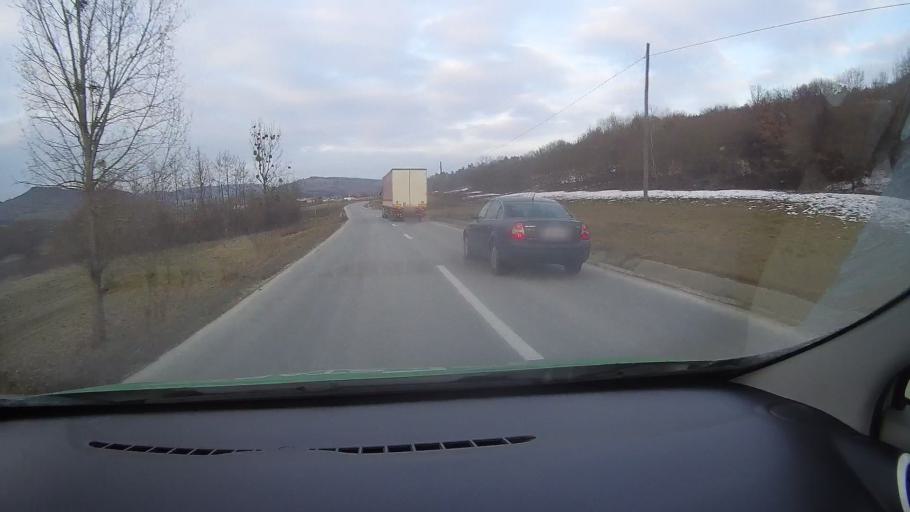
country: RO
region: Harghita
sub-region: Comuna Simonesti
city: Simonesti
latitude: 46.3479
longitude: 25.1251
